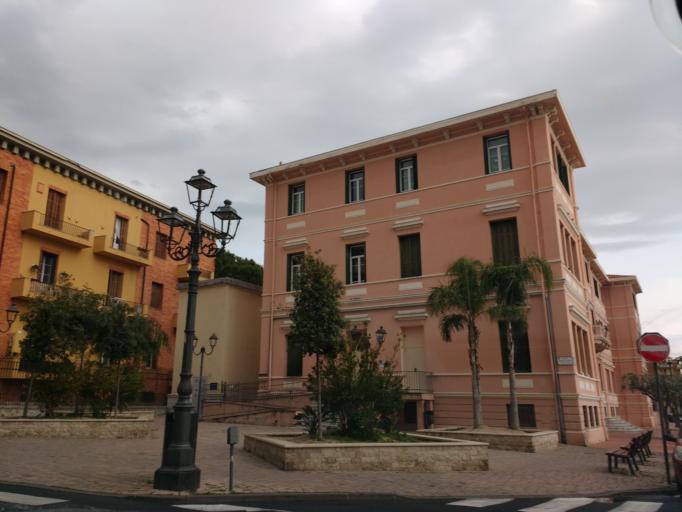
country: IT
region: Liguria
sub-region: Provincia di Imperia
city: Ventimiglia
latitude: 43.7885
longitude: 7.6114
